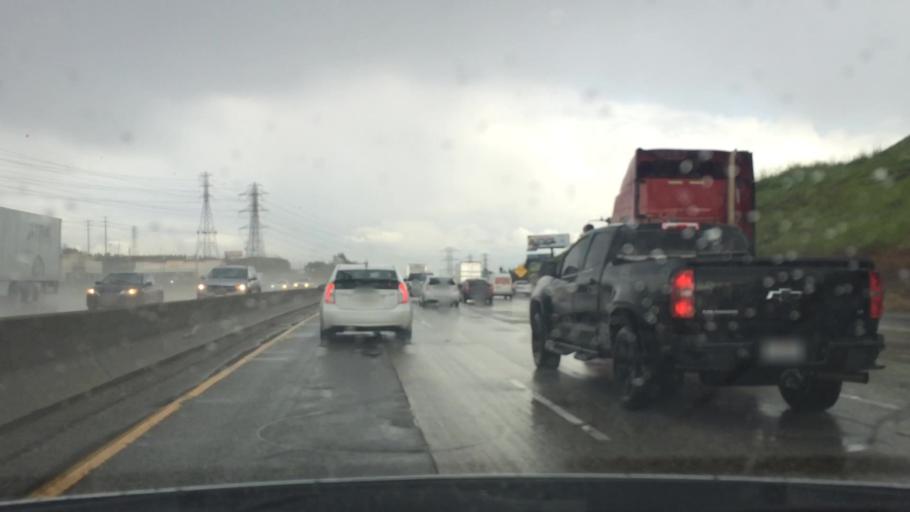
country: US
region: California
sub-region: Los Angeles County
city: Montebello
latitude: 34.0363
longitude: -118.1012
